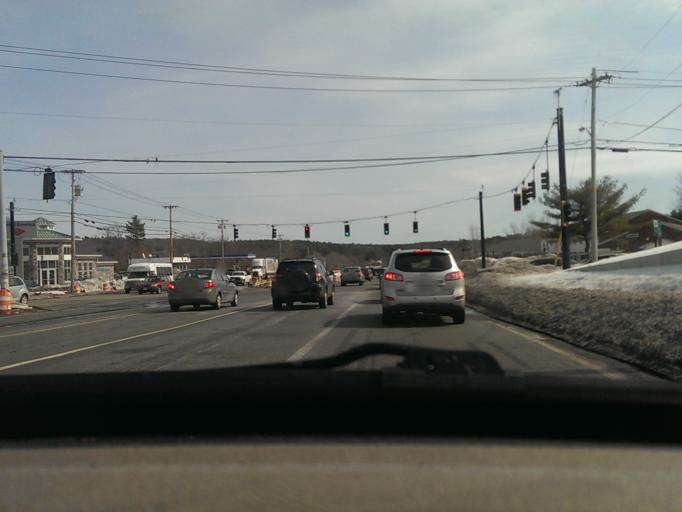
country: US
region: Massachusetts
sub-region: Worcester County
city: Sutton
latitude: 42.1616
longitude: -71.7393
